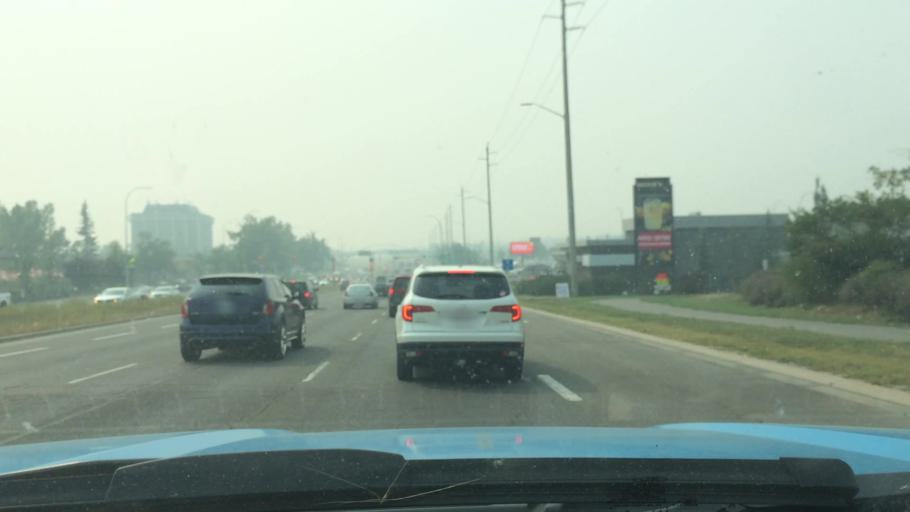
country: CA
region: Alberta
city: Calgary
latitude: 50.9591
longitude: -114.0719
